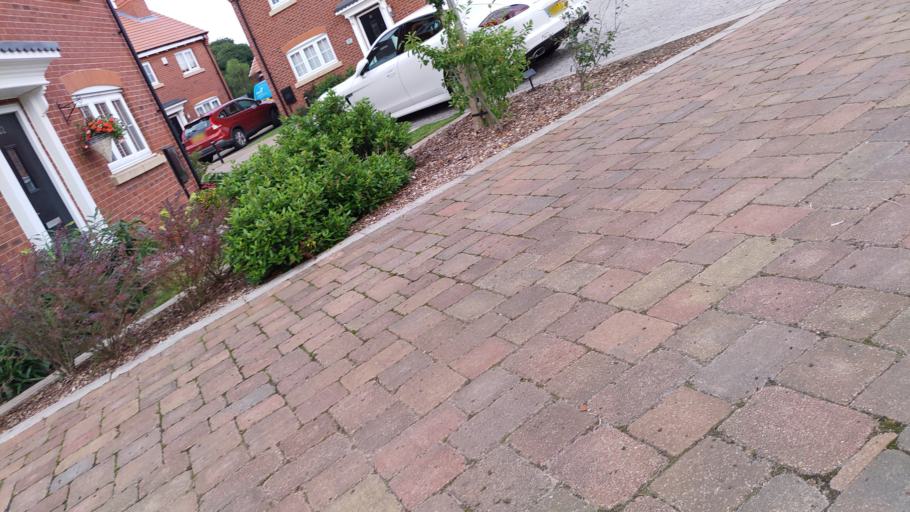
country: GB
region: England
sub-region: Lancashire
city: Coppull
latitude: 53.6292
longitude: -2.6362
